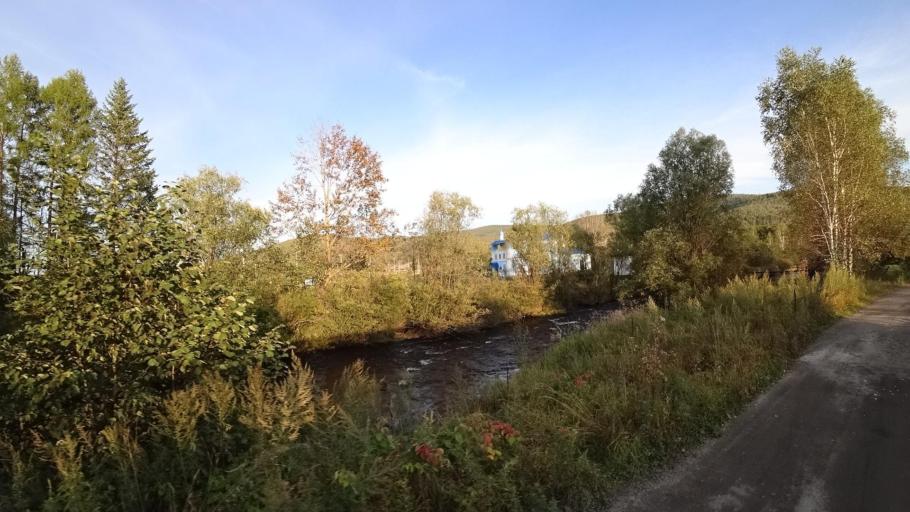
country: RU
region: Jewish Autonomous Oblast
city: Kul'dur
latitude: 49.1998
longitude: 131.6283
